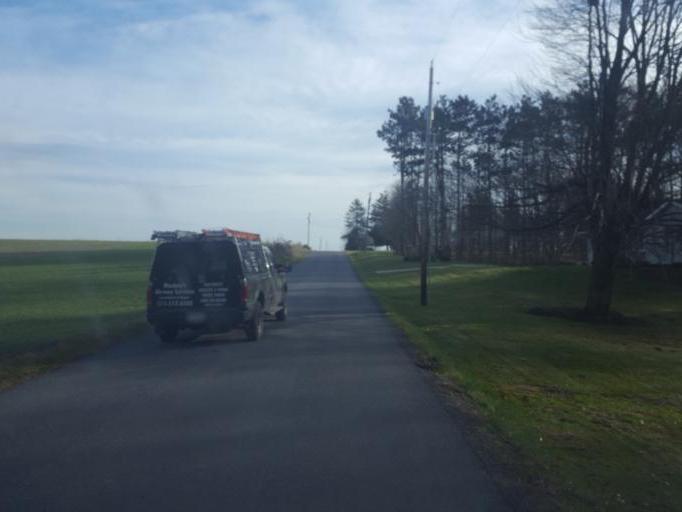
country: US
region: Ohio
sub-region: Knox County
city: Fredericktown
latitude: 40.5302
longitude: -82.5659
